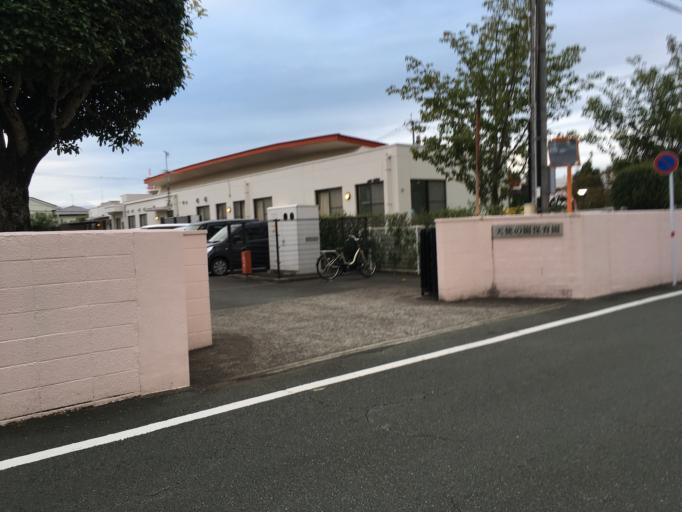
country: JP
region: Kumamoto
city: Kumamoto
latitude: 32.8056
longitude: 130.7342
